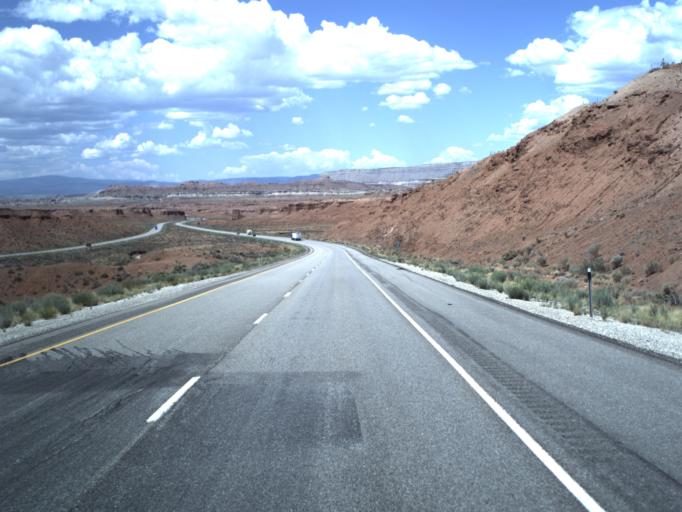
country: US
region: Utah
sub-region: Emery County
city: Ferron
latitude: 38.8476
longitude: -111.0264
